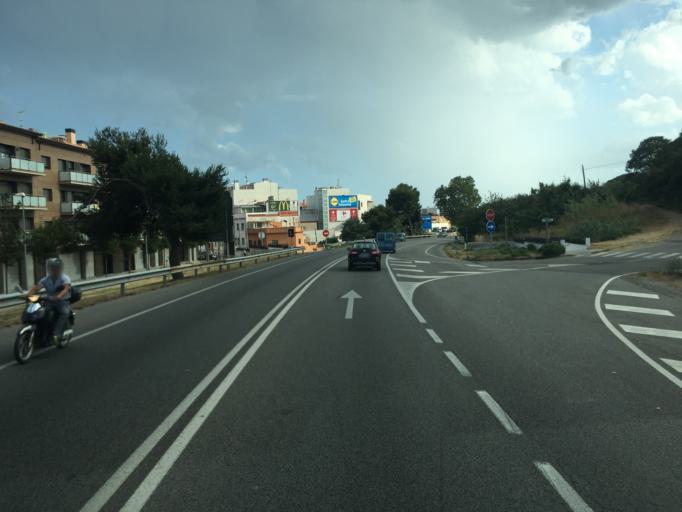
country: ES
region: Catalonia
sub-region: Provincia de Barcelona
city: Malgrat de Mar
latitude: 41.6510
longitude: 2.7354
